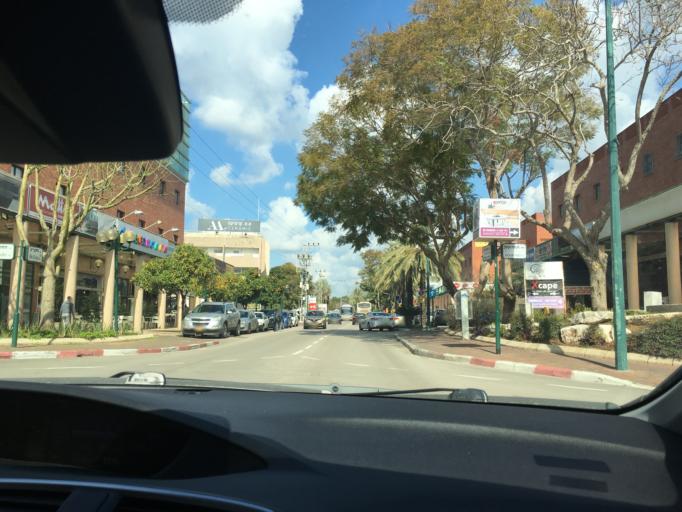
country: IL
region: Central District
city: Kfar Saba
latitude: 32.1768
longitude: 34.9273
